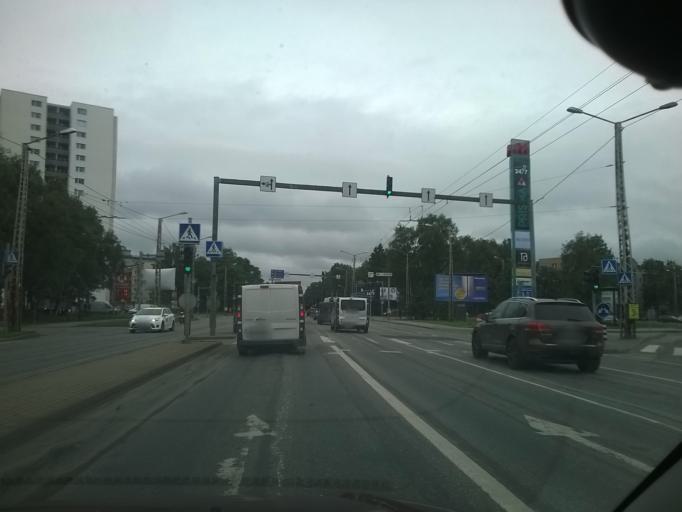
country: EE
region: Harju
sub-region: Tallinna linn
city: Tallinn
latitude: 59.4093
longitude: 24.6859
